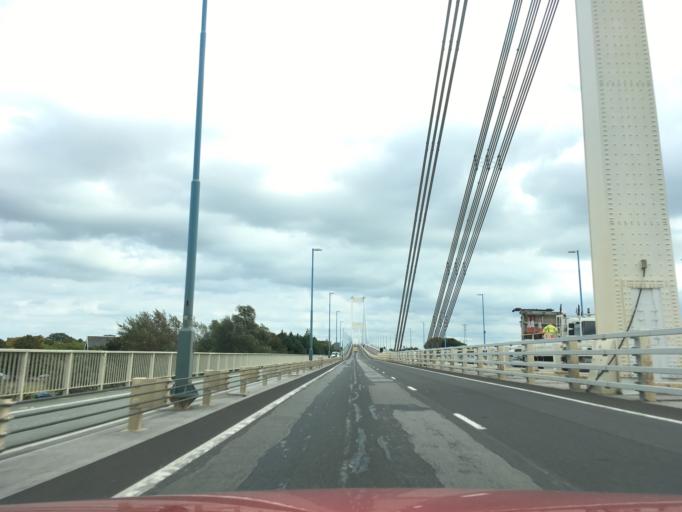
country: GB
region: Wales
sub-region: Monmouthshire
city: Chepstow
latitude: 51.6173
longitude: -2.6596
